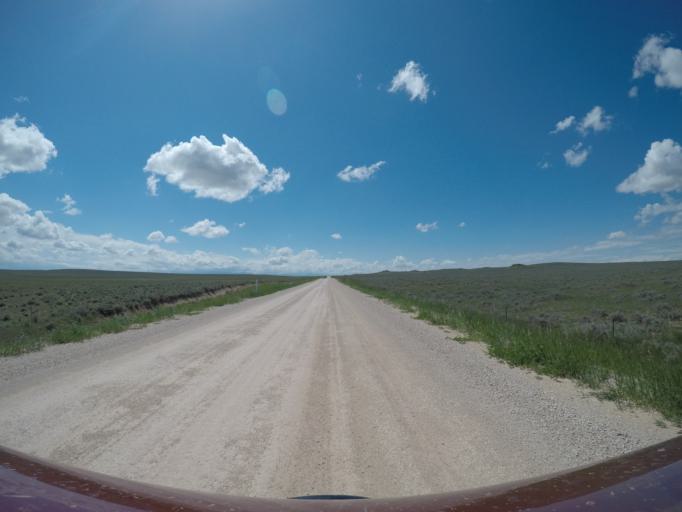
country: US
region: Wyoming
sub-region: Park County
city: Powell
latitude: 45.2051
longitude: -108.7465
